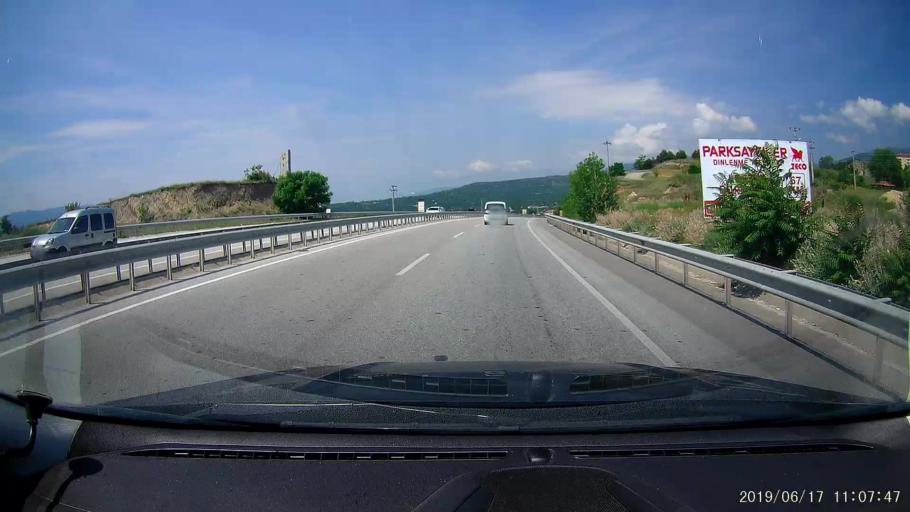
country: TR
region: Kastamonu
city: Tosya
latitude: 40.9993
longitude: 34.0496
